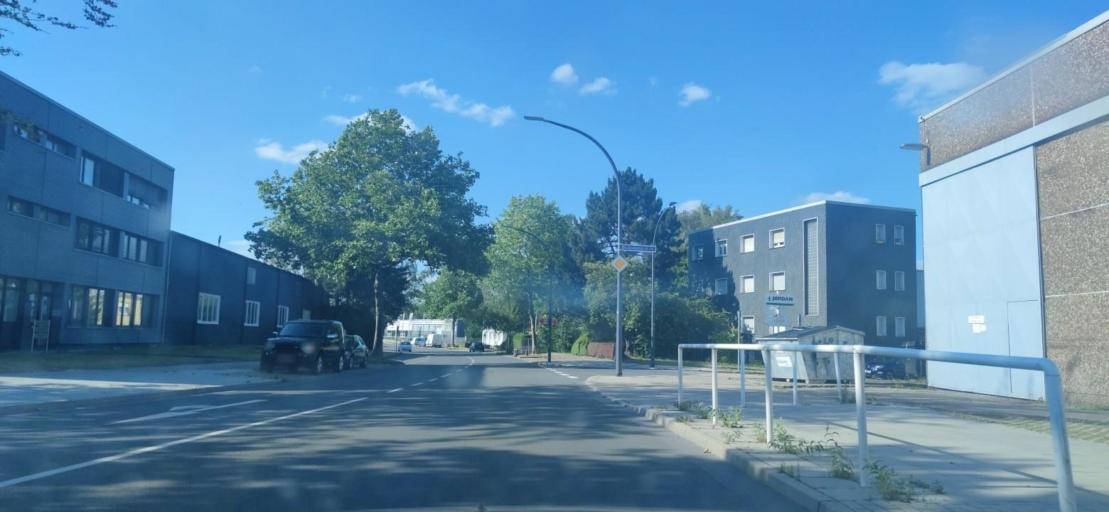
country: DE
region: North Rhine-Westphalia
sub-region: Regierungsbezirk Dusseldorf
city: Essen
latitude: 51.4697
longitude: 7.0544
